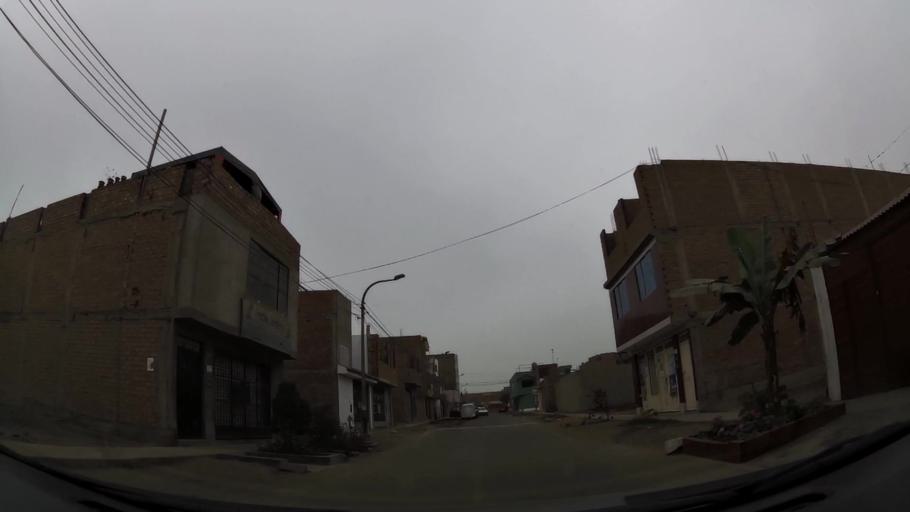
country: PE
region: Lima
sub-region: Lima
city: Urb. Santo Domingo
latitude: -11.8863
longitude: -77.0405
